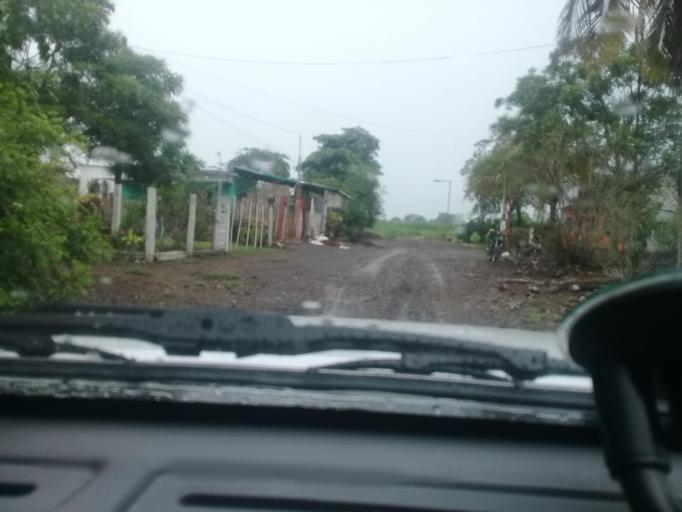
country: MX
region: Veracruz
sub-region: Puente Nacional
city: Cabezas
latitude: 19.3568
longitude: -96.3773
